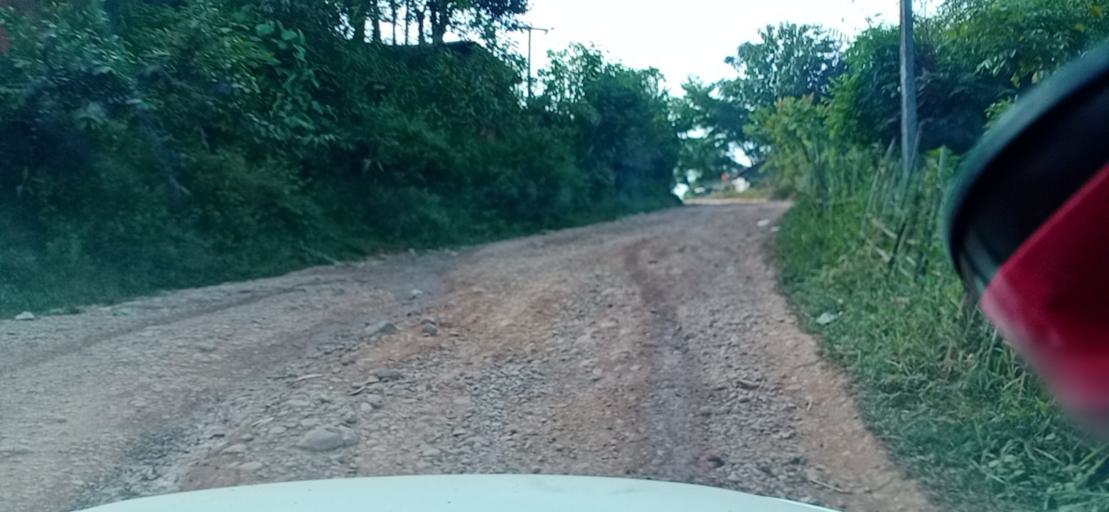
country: TH
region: Changwat Bueng Kan
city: Pak Khat
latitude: 18.6795
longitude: 103.1893
